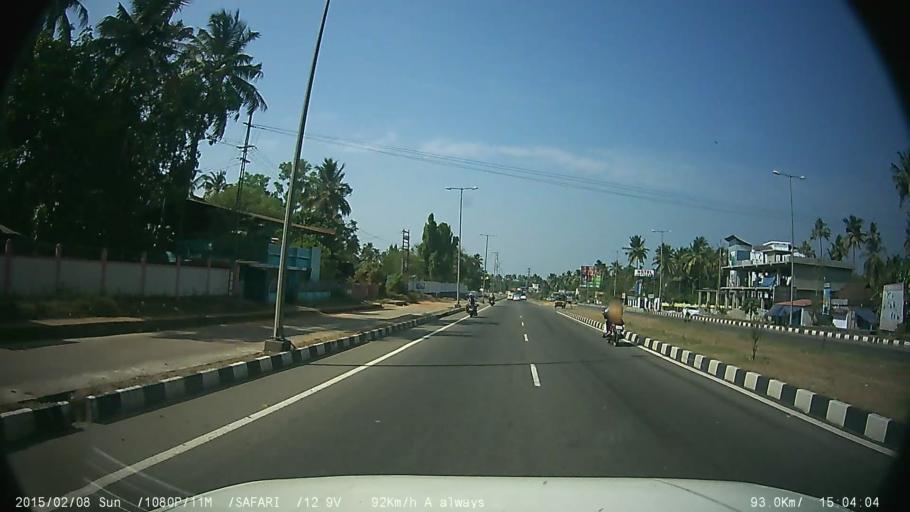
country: IN
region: Kerala
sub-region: Thrissur District
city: Kizhake Chalakudi
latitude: 10.3435
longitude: 76.3220
